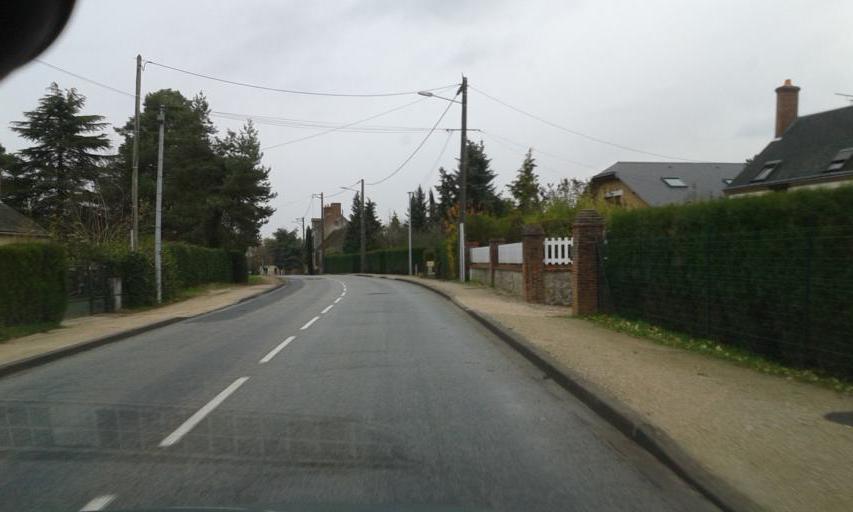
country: FR
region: Centre
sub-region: Departement du Loiret
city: Vitry-aux-Loges
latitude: 47.9322
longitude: 2.2624
